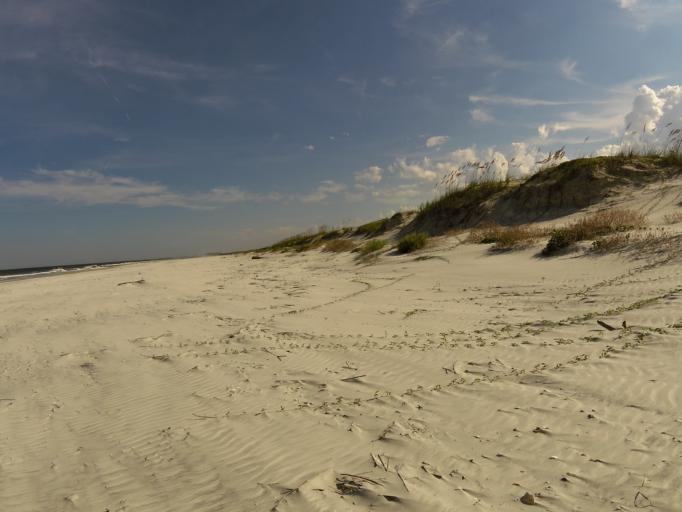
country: US
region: Florida
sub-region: Duval County
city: Atlantic Beach
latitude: 30.4517
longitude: -81.4105
